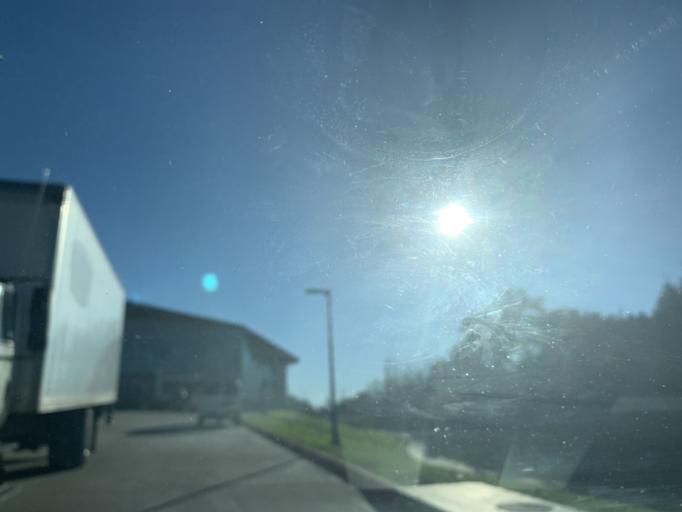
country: US
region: Texas
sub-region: Travis County
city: Wells Branch
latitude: 30.4012
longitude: -97.7123
